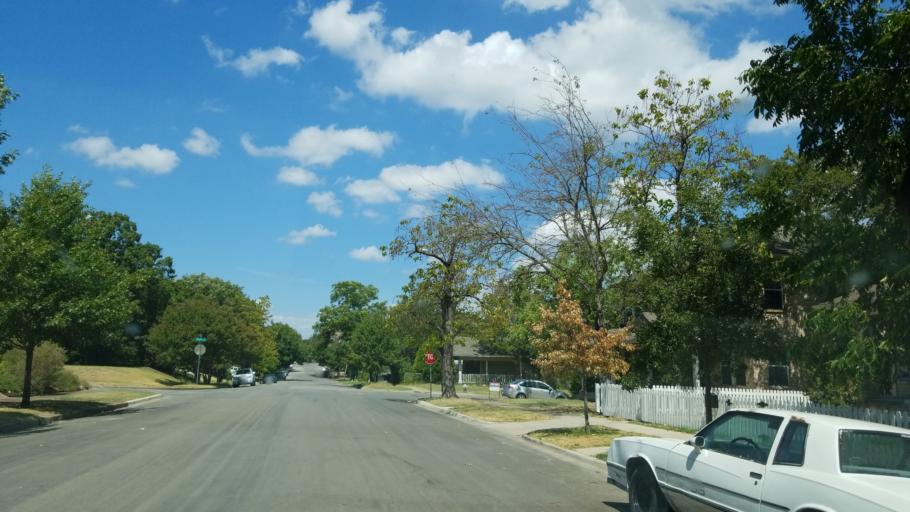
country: US
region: Texas
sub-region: Dallas County
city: Dallas
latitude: 32.7533
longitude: -96.8266
